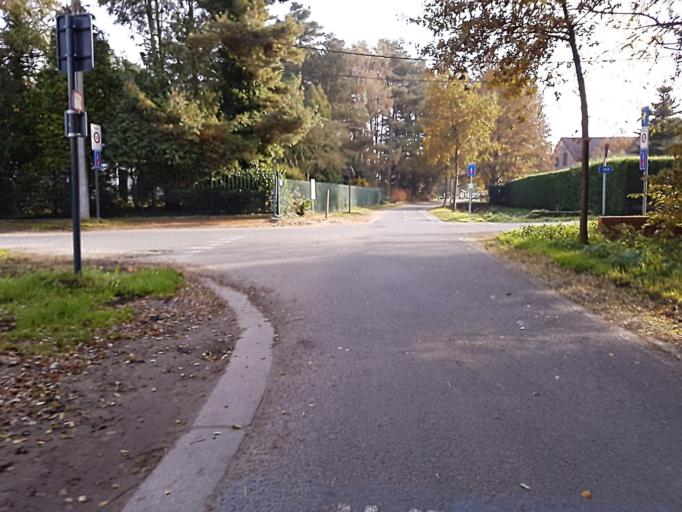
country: BE
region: Flanders
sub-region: Provincie Antwerpen
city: Bonheiden
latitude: 51.0364
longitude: 4.5595
